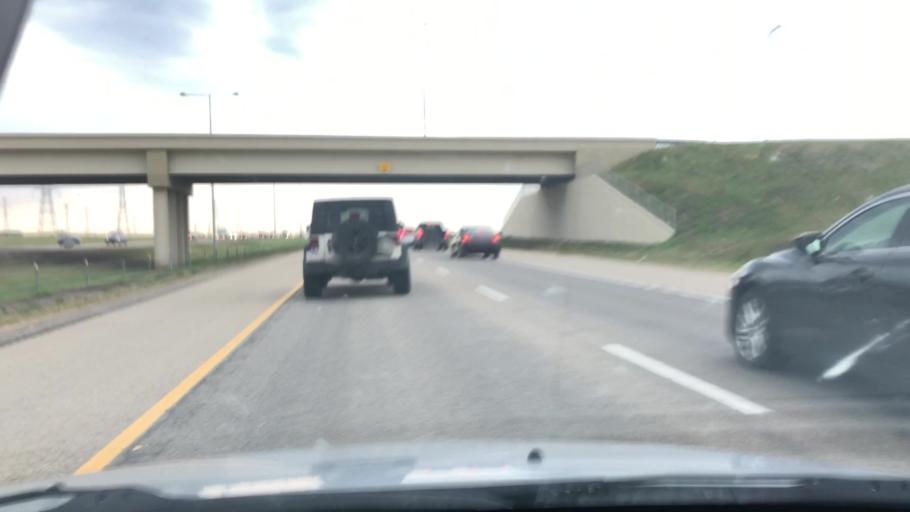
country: CA
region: Alberta
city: Beaumont
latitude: 53.4357
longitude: -113.3930
